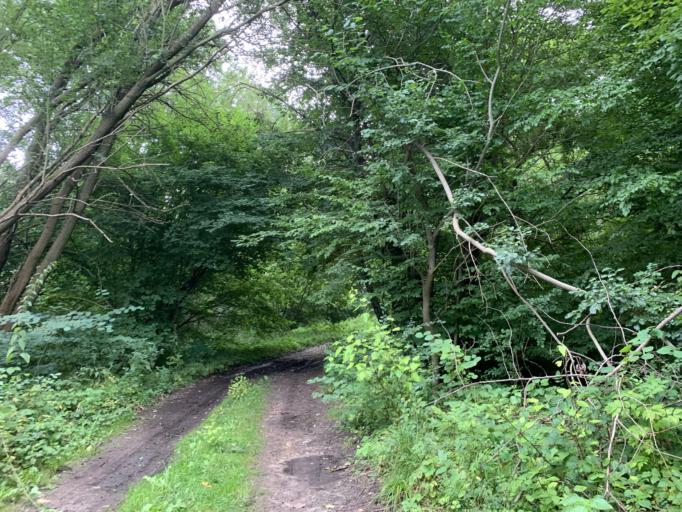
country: DE
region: Mecklenburg-Vorpommern
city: Gross Nemerow
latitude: 53.4255
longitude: 13.1882
